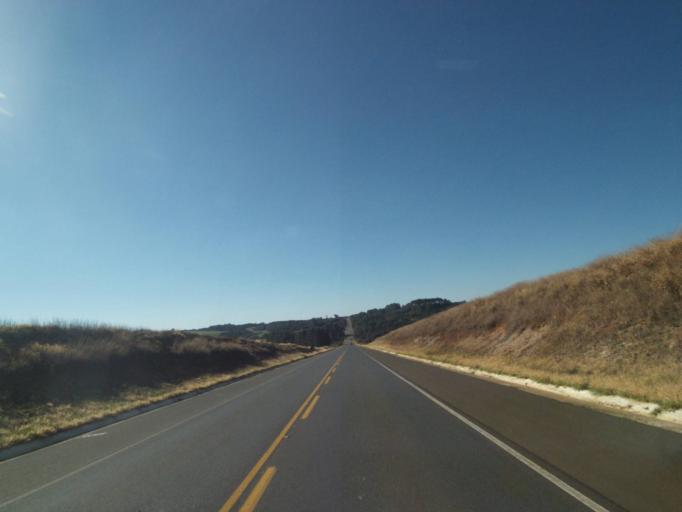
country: BR
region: Parana
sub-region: Tibagi
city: Tibagi
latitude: -24.6170
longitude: -50.4478
